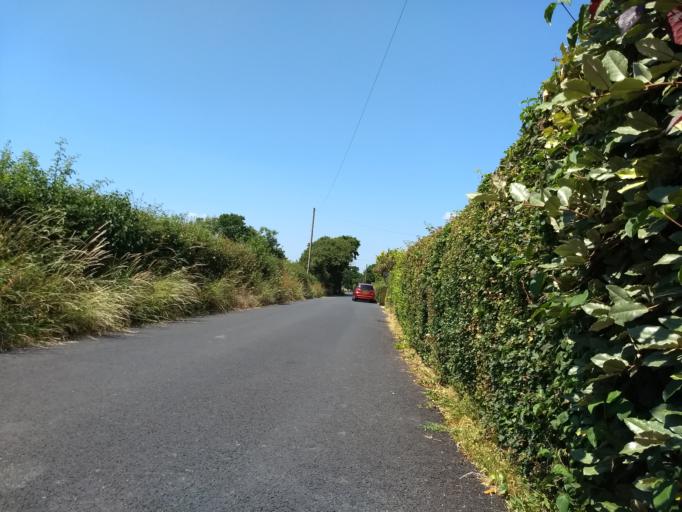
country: GB
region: England
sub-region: Isle of Wight
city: Shalfleet
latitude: 50.7146
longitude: -1.3633
